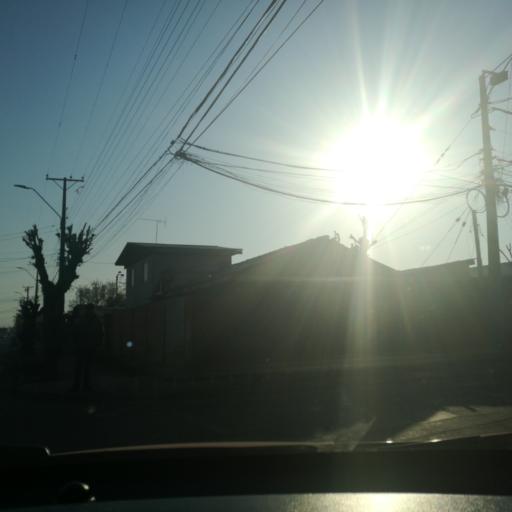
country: CL
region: O'Higgins
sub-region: Provincia de Cachapoal
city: Rancagua
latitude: -34.1707
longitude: -70.7115
